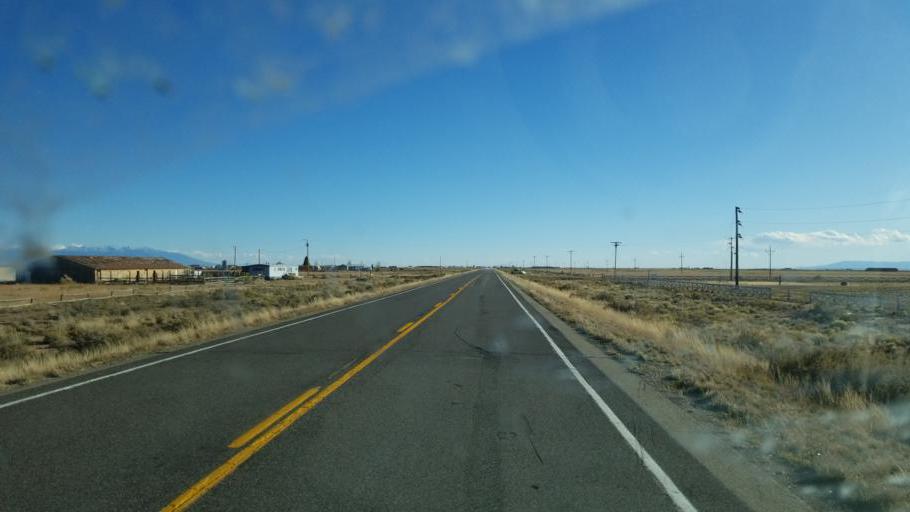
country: US
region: Colorado
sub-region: Saguache County
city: Saguache
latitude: 38.1317
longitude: -105.9232
